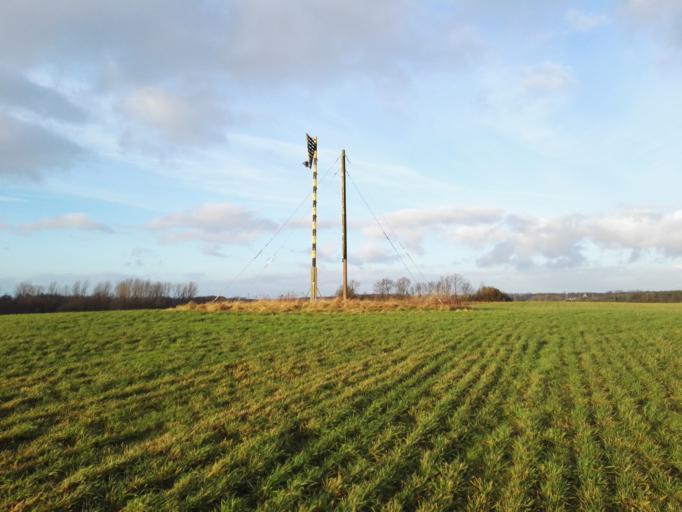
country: DK
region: Capital Region
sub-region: Frederikssund Kommune
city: Jaegerspris
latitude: 55.8443
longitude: 11.9725
